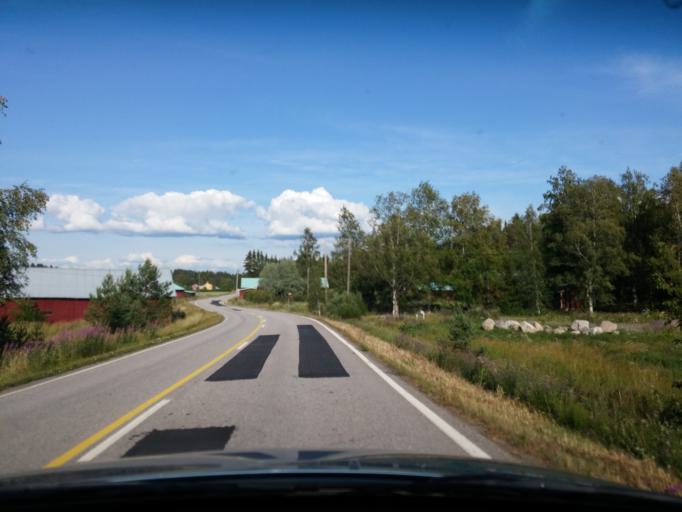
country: FI
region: Uusimaa
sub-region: Porvoo
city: Askola
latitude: 60.5163
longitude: 25.5186
